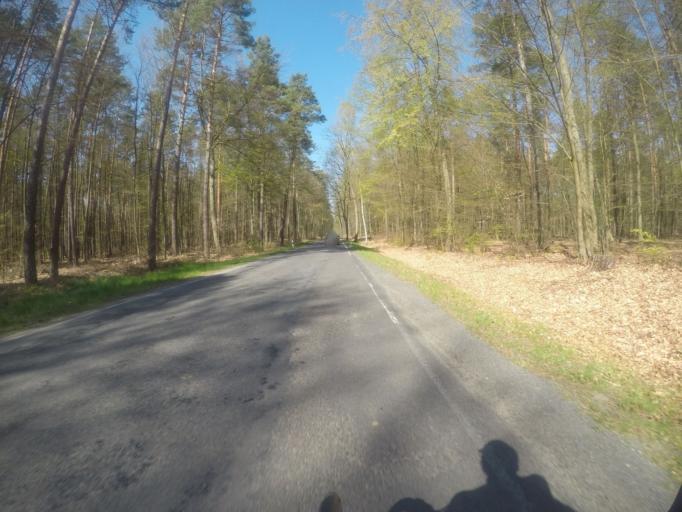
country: DE
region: Brandenburg
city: Rudnitz
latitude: 52.7471
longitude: 13.5680
